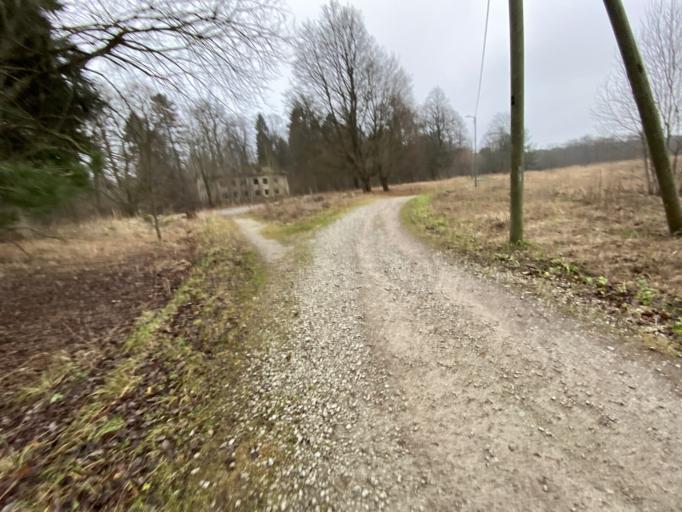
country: EE
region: Harju
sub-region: Tallinna linn
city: Kose
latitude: 59.4631
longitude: 24.8471
